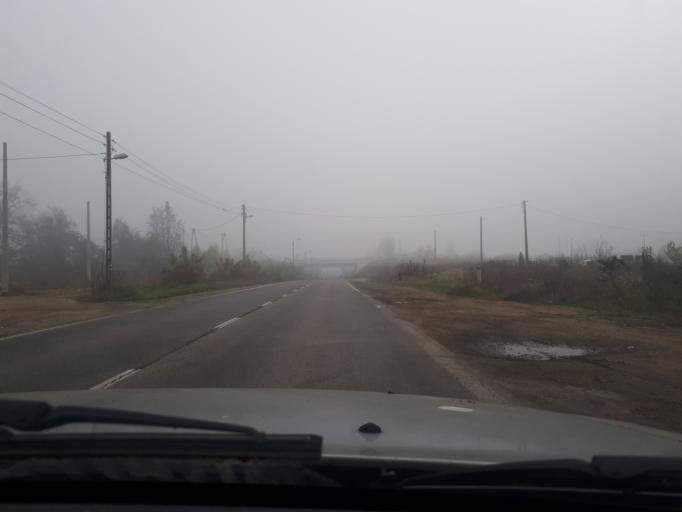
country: PL
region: Lesser Poland Voivodeship
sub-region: Powiat wielicki
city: Podleze
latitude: 50.0783
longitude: 20.1667
